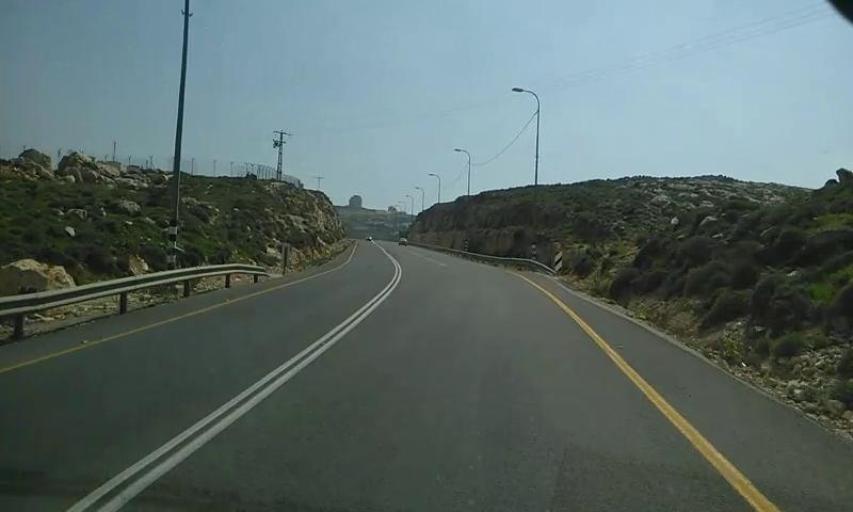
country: PS
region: West Bank
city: Jaba`
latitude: 31.8682
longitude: 35.2582
